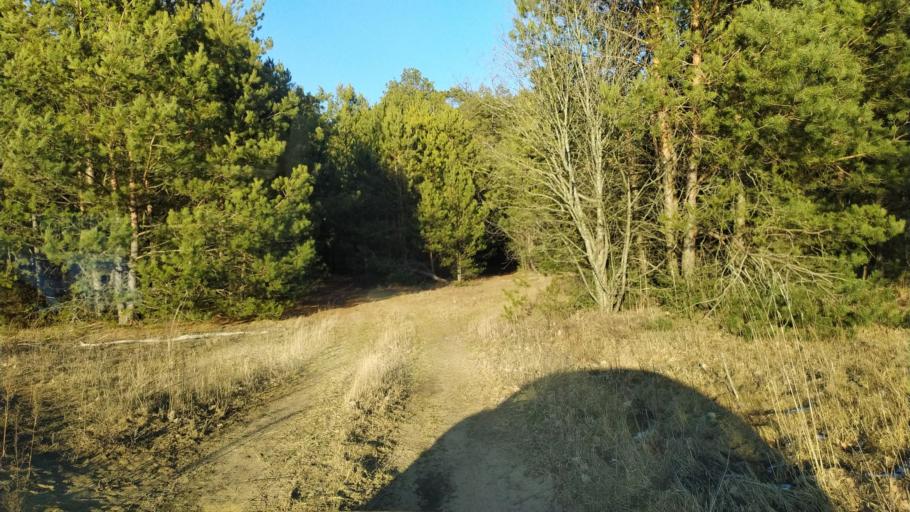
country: BY
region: Brest
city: Pruzhany
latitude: 52.5467
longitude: 24.2726
